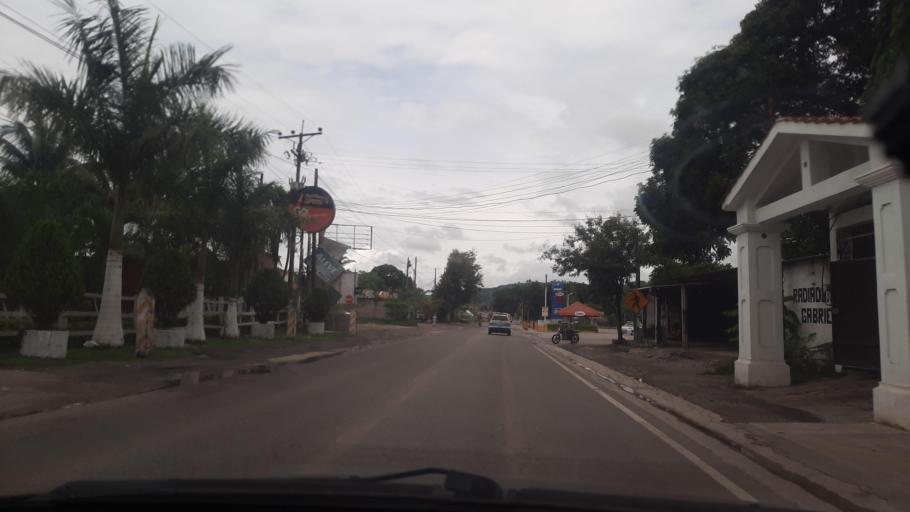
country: GT
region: Izabal
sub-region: Municipio de Los Amates
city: Los Amates
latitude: 15.2540
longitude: -89.1012
